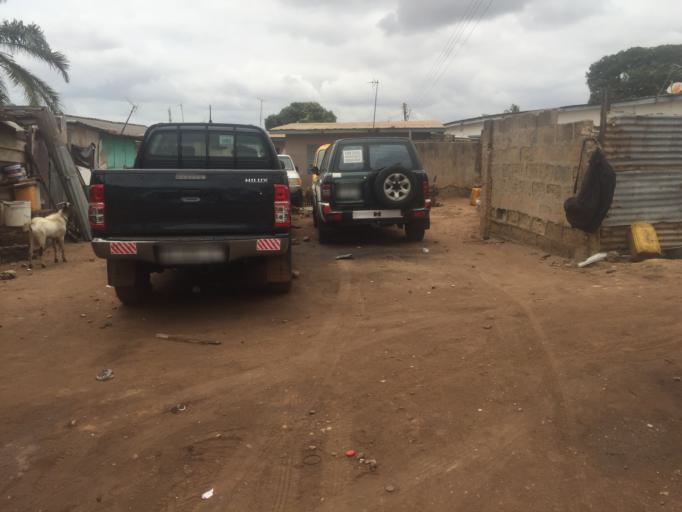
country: GH
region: Greater Accra
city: Dome
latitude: 5.6033
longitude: -0.2441
